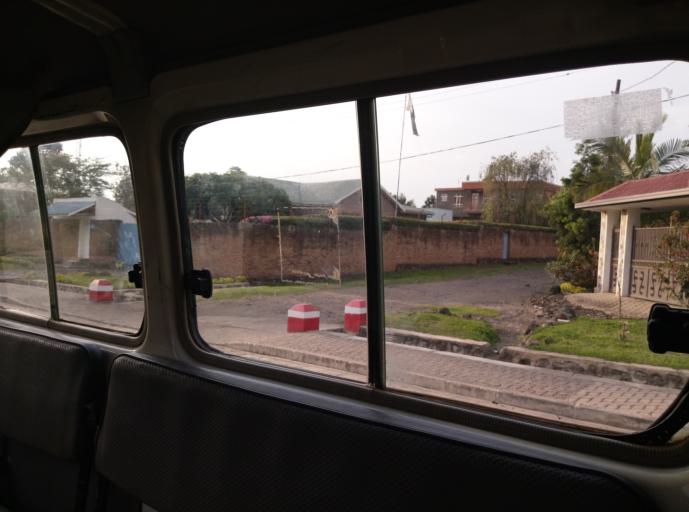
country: RW
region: Western Province
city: Gisenyi
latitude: -1.6955
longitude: 29.2529
